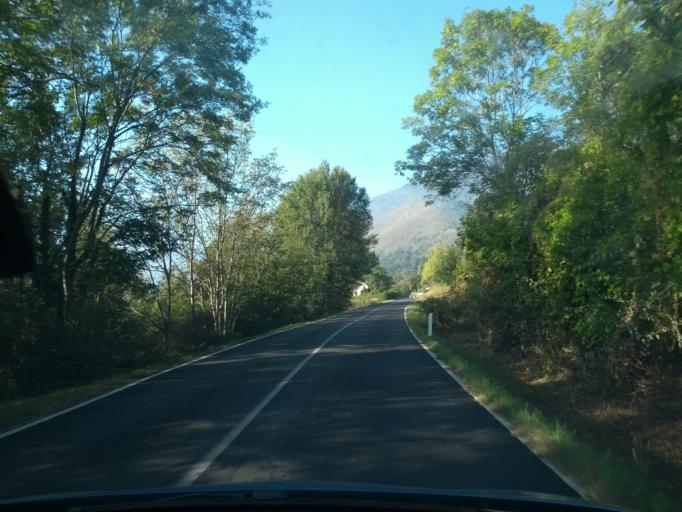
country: IT
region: Piedmont
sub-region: Provincia di Torino
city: Vallo Torinese
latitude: 45.2288
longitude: 7.5025
